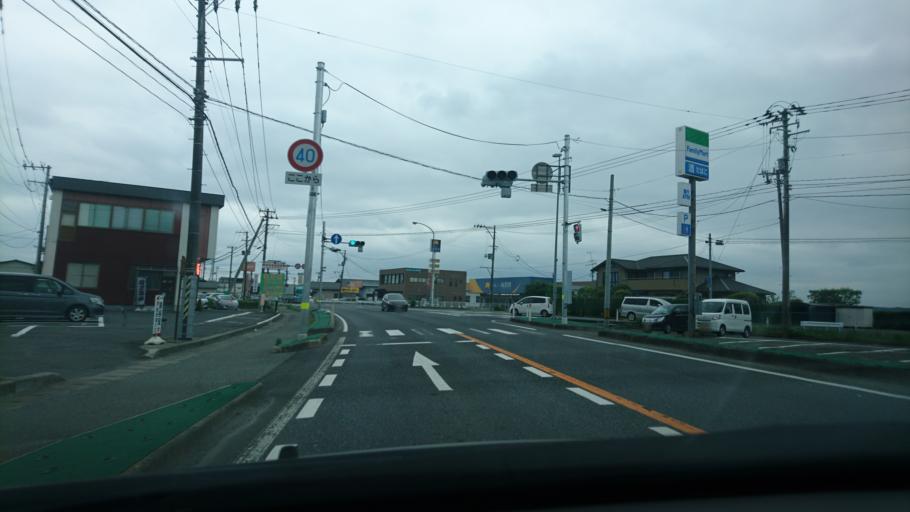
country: JP
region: Miyagi
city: Furukawa
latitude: 38.7490
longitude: 141.0145
